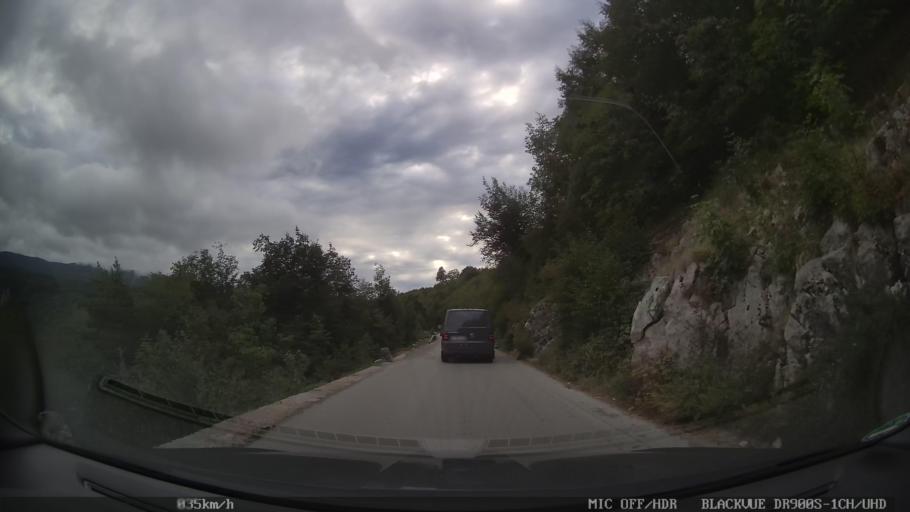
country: HR
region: Licko-Senjska
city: Jezerce
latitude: 44.9238
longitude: 15.6075
